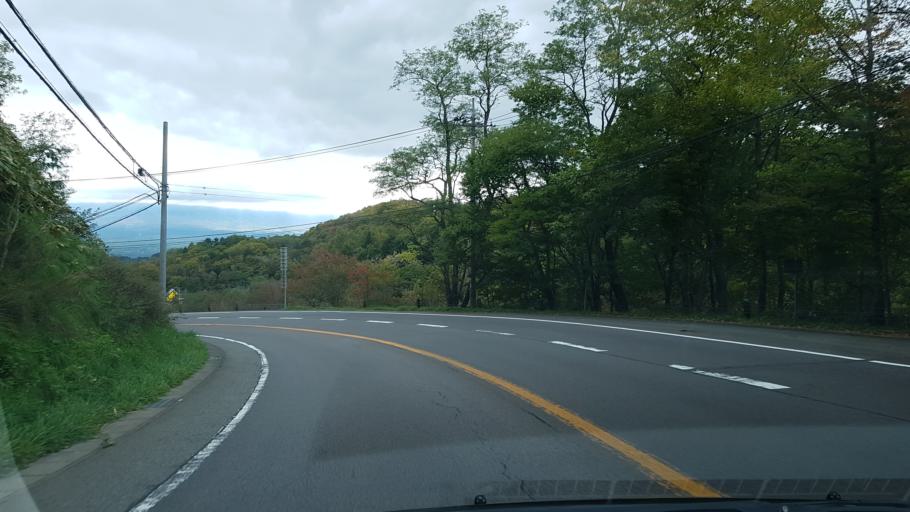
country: JP
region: Gunma
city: Nakanojomachi
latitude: 36.5994
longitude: 138.5868
